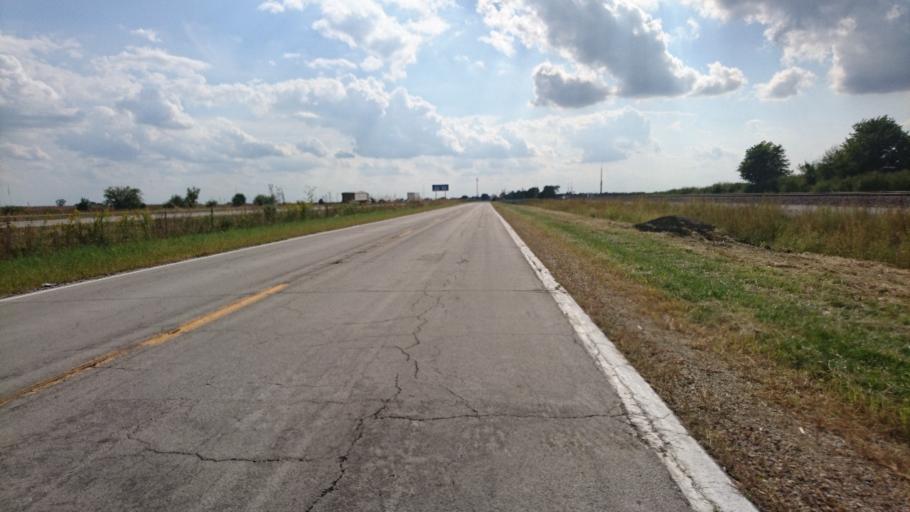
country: US
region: Illinois
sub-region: Logan County
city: Atlanta
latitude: 40.3353
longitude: -89.1451
